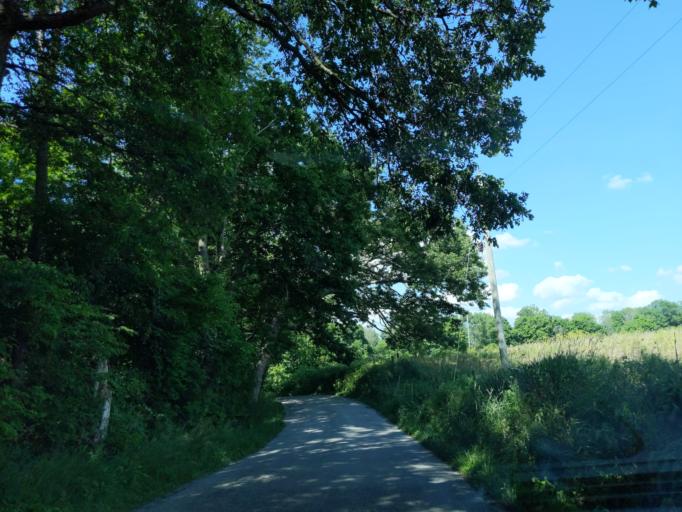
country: US
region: Indiana
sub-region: Ripley County
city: Osgood
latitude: 39.1985
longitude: -85.4171
